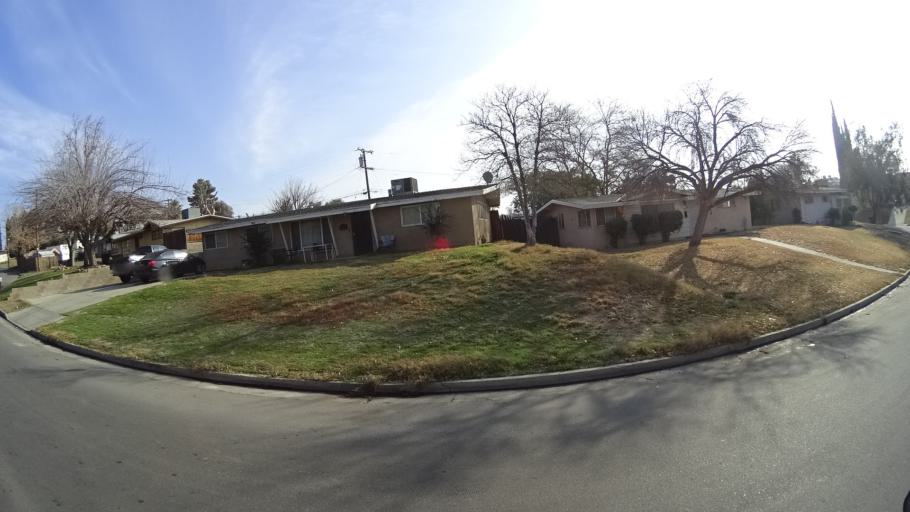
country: US
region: California
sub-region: Kern County
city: Oildale
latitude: 35.4024
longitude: -118.9842
